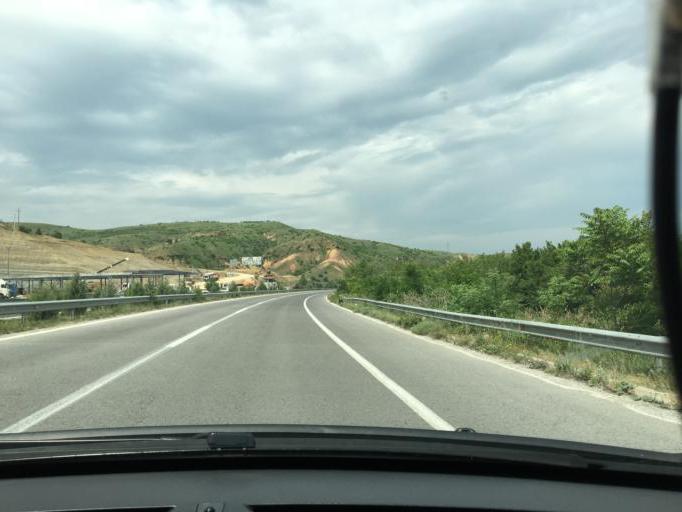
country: MK
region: Demir Kapija
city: Demir Kapija
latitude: 41.4253
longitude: 22.1877
